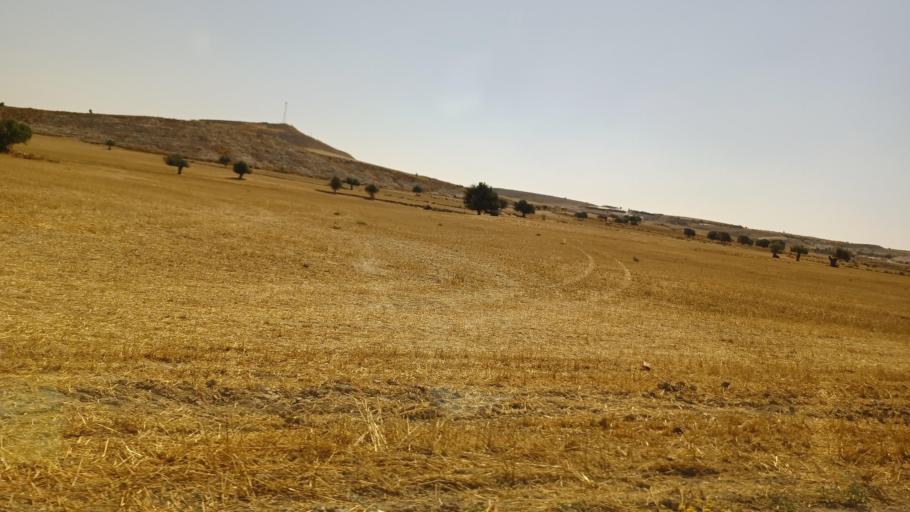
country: CY
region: Larnaka
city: Athienou
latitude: 35.0329
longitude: 33.5117
